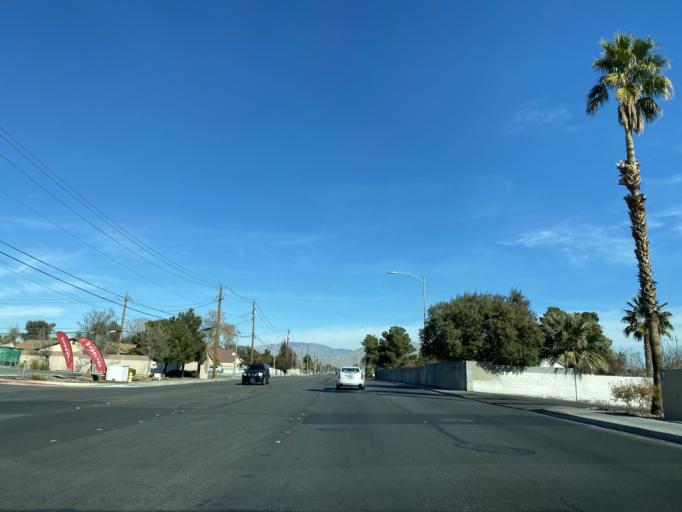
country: US
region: Nevada
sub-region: Clark County
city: Las Vegas
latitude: 36.2181
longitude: -115.2258
